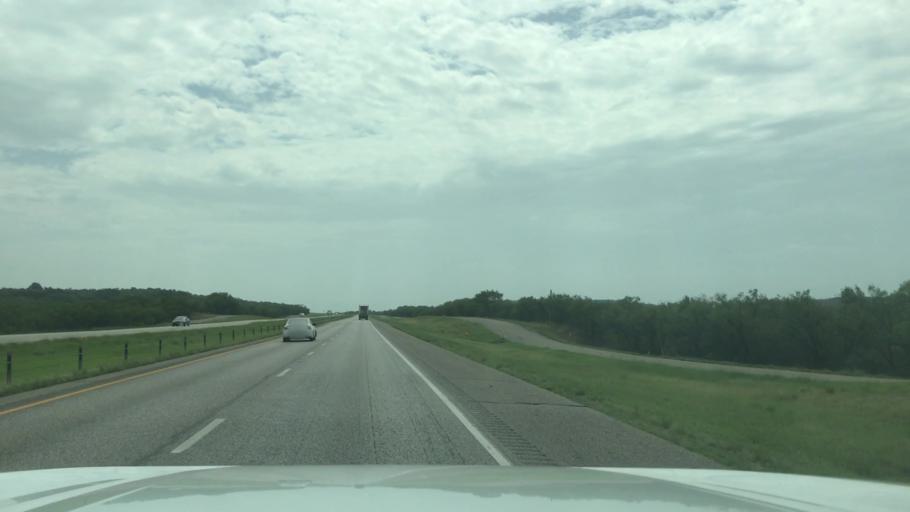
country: US
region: Texas
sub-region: Callahan County
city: Baird
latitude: 32.3730
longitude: -99.2296
